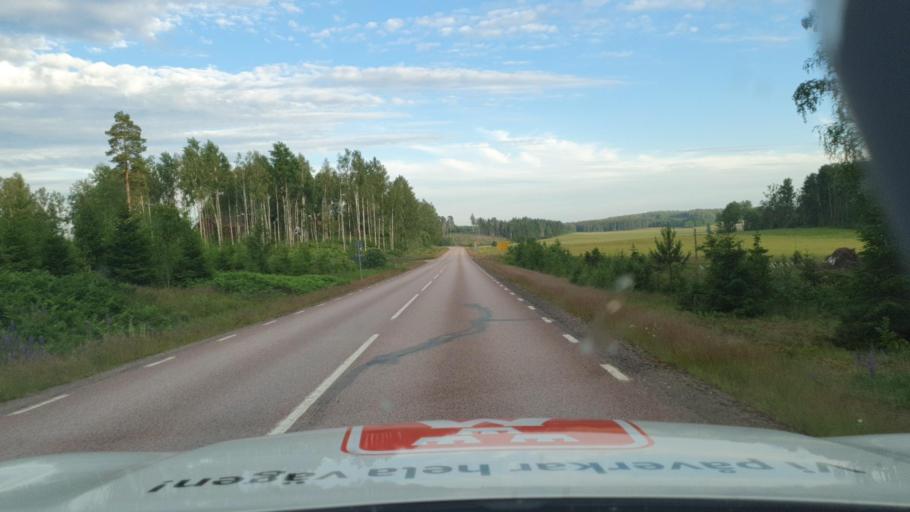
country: SE
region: Vaermland
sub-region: Karlstads Kommun
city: Molkom
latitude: 59.4747
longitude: 13.8083
